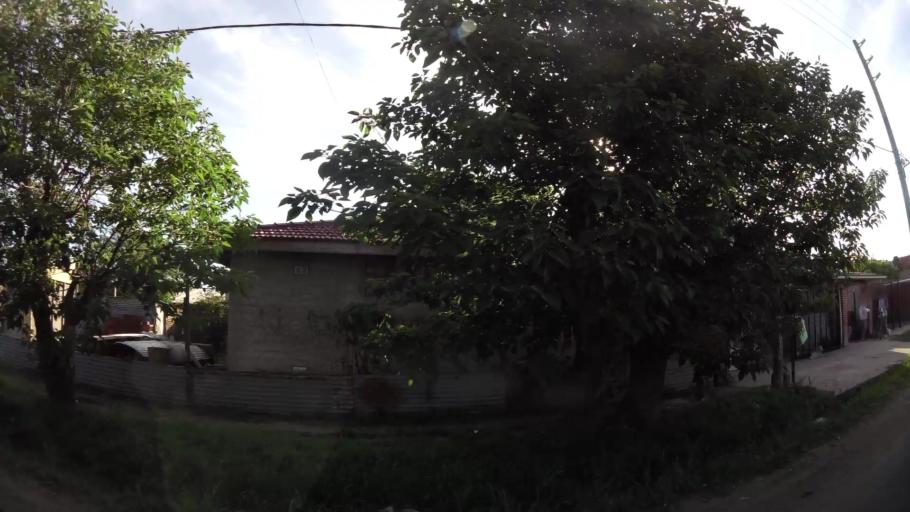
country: AR
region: Buenos Aires
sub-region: Partido de Almirante Brown
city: Adrogue
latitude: -34.8154
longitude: -58.3244
